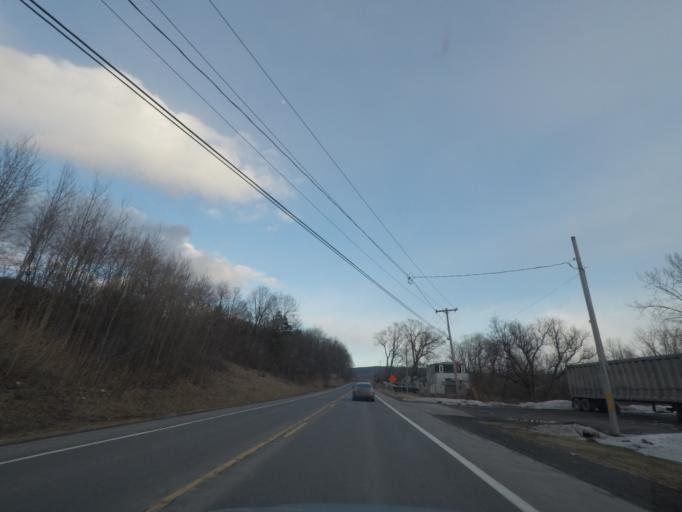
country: US
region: New York
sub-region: Herkimer County
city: Ilion
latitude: 43.0256
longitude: -75.0379
